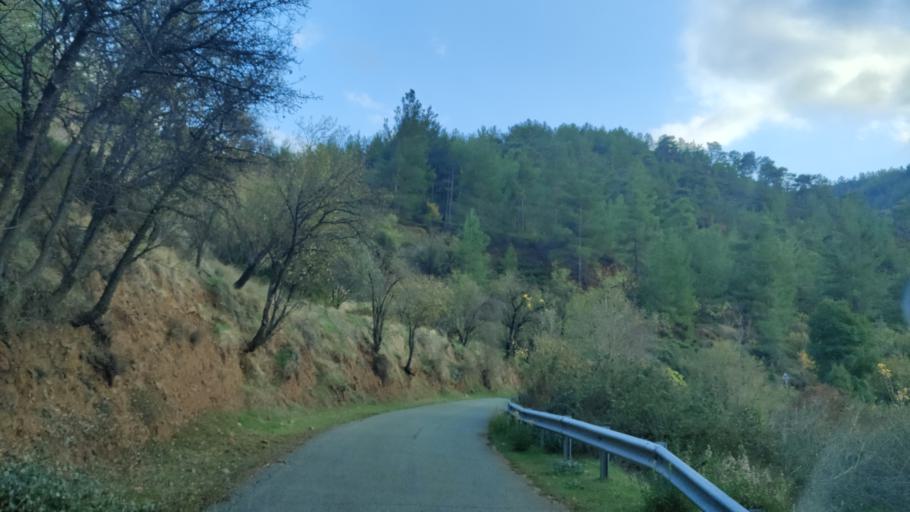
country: CY
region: Lefkosia
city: Lefka
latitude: 35.0723
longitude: 32.7422
